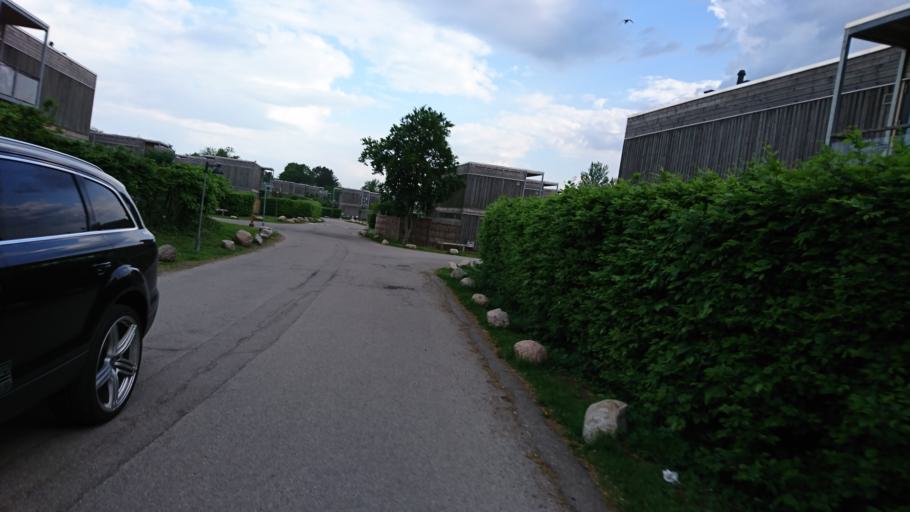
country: DK
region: Capital Region
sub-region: Fureso Kommune
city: Vaerlose
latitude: 55.7569
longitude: 12.3960
